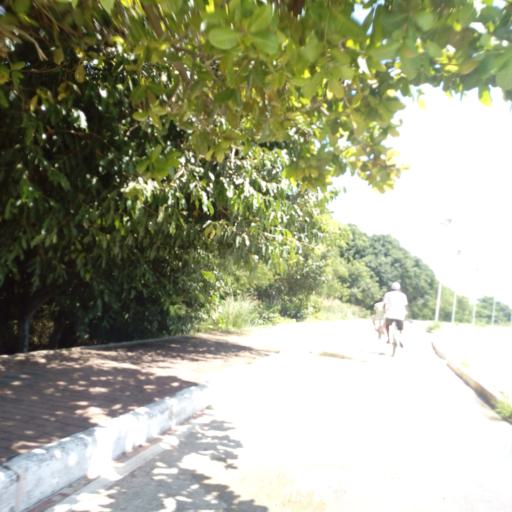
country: BR
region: Pernambuco
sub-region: Ipojuca
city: Ipojuca
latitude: -8.5143
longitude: -35.0099
